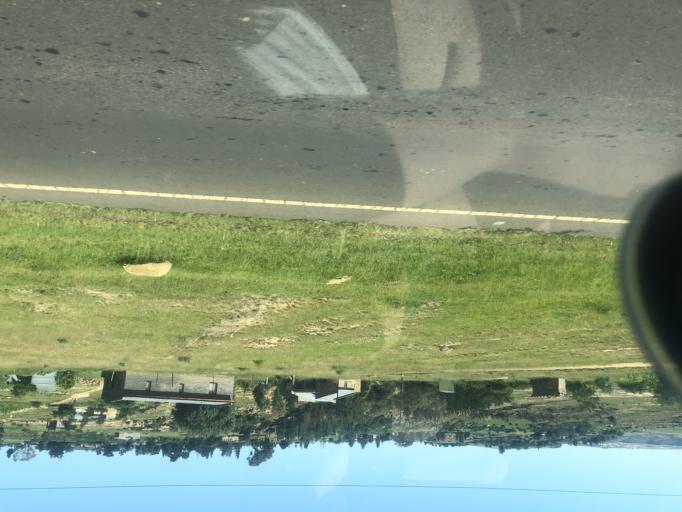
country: LS
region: Maseru
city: Maseru
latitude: -29.3712
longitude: 27.6353
